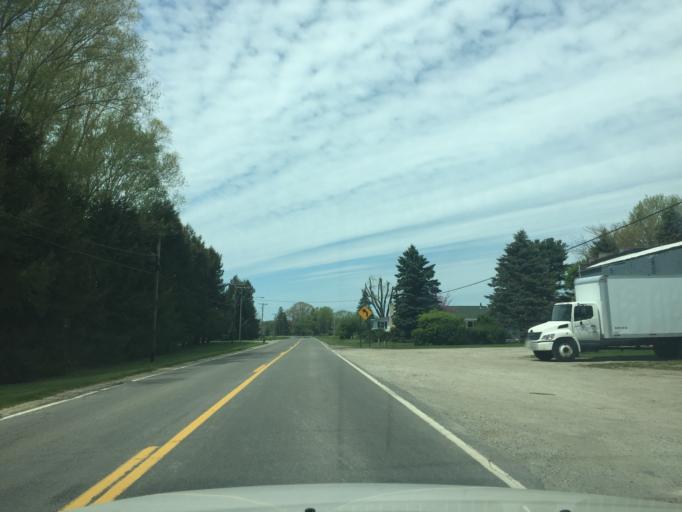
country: US
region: Michigan
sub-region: Berrien County
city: Stevensville
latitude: 41.9917
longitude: -86.5052
